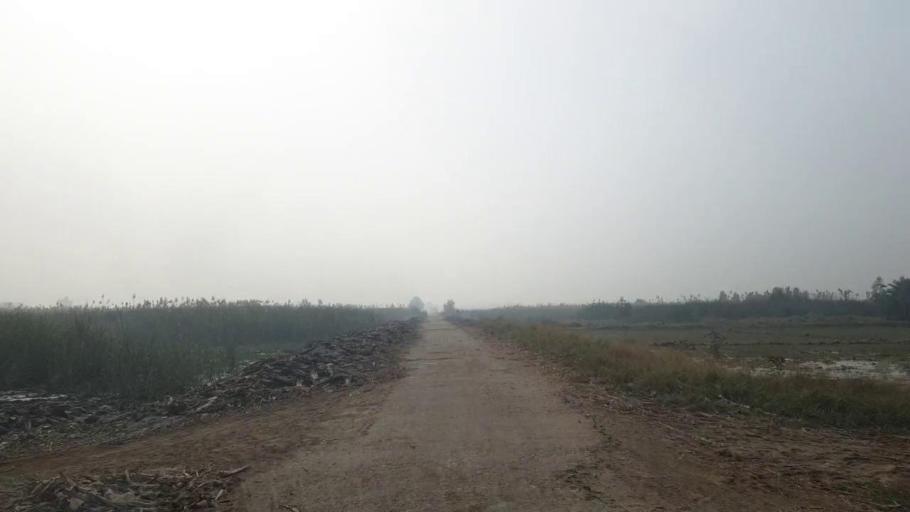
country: PK
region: Sindh
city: Tando Adam
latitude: 25.7789
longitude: 68.6073
